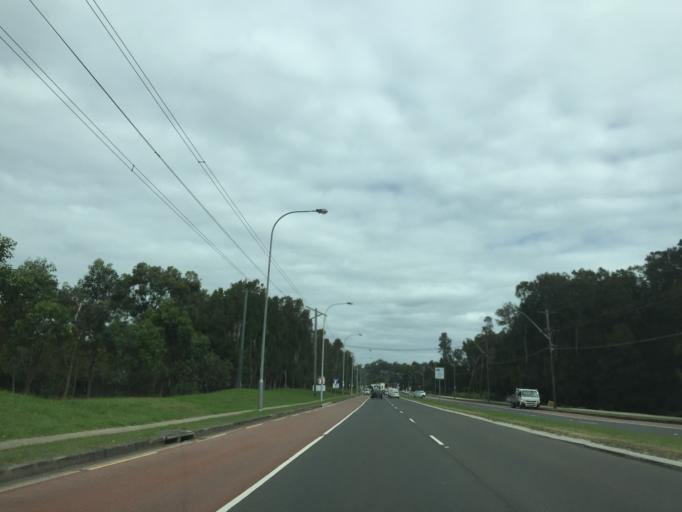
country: AU
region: New South Wales
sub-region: Pittwater
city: Warriewood
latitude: -33.6944
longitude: 151.3032
